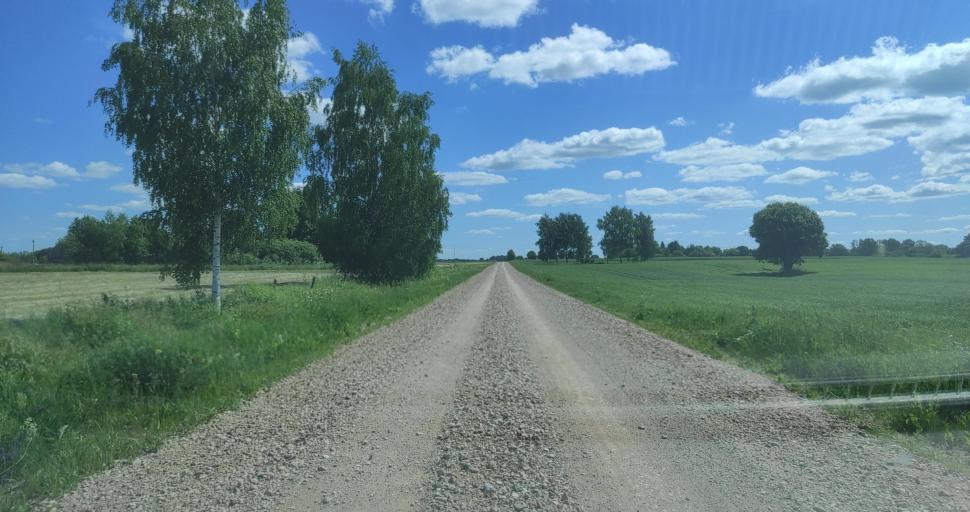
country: LV
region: Aizpute
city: Aizpute
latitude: 56.8384
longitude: 21.7305
